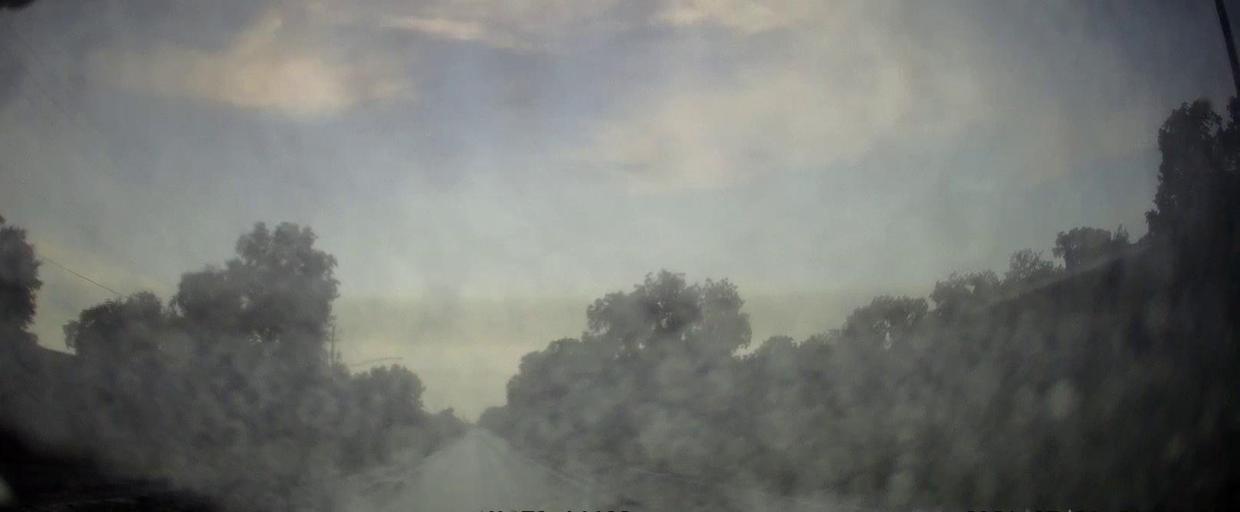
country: US
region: Georgia
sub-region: Dodge County
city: Chester
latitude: 32.5602
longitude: -83.1552
